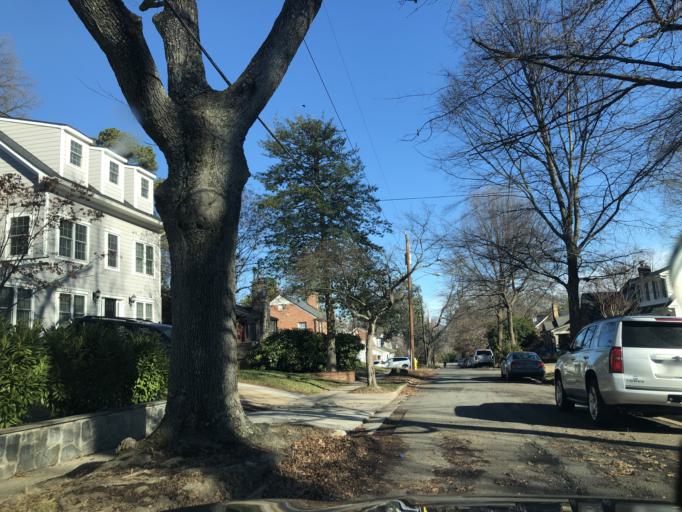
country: US
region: Virginia
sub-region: Arlington County
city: Arlington
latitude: 38.8858
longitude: -77.1236
